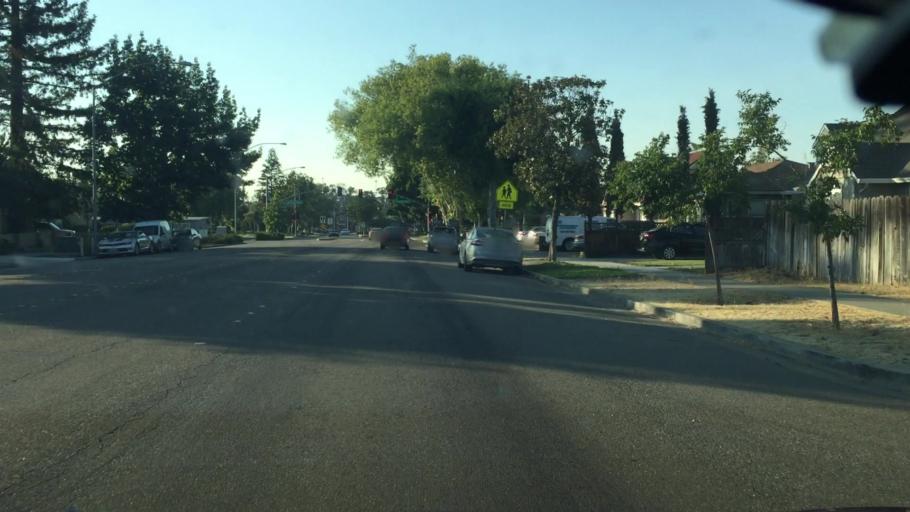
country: US
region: California
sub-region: Alameda County
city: Livermore
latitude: 37.6884
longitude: -121.7718
